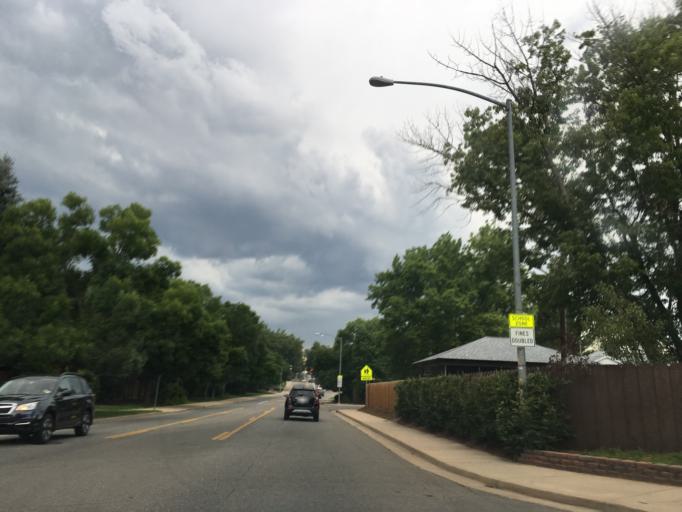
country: US
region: Colorado
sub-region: Arapahoe County
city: Glendale
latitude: 39.7111
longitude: -104.9555
